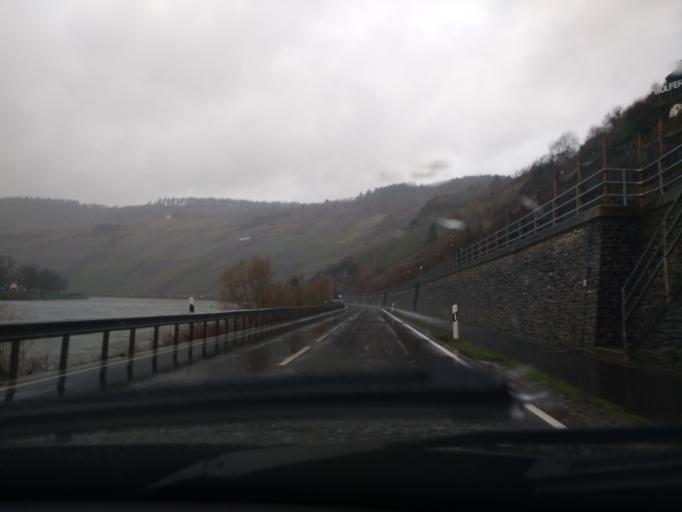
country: DE
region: Rheinland-Pfalz
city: Enkirch
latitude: 49.9797
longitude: 7.1081
